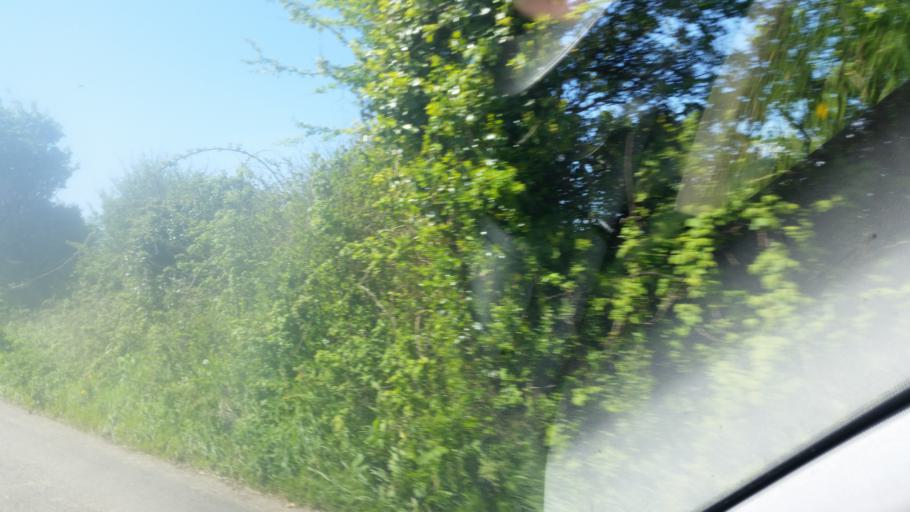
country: IE
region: Munster
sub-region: Waterford
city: Dunmore East
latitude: 52.1886
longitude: -6.8569
